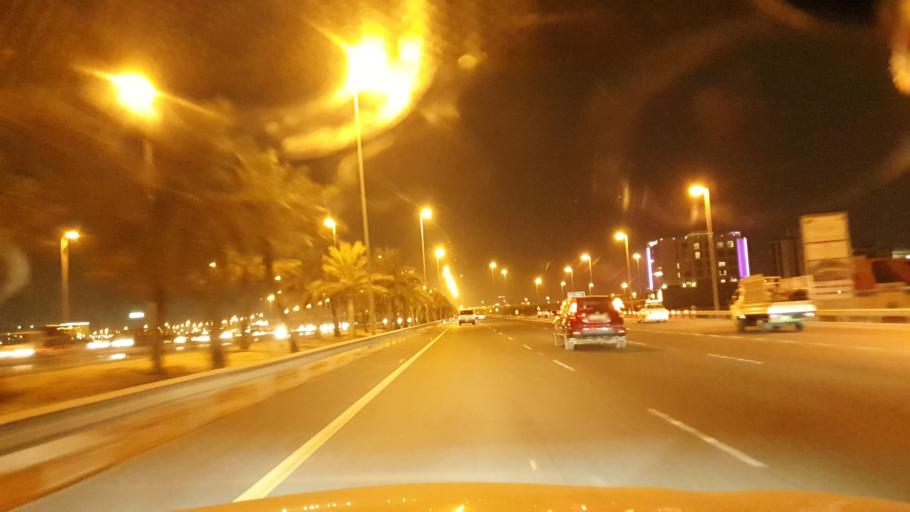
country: BH
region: Northern
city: Madinat `Isa
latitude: 26.1895
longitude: 50.5093
